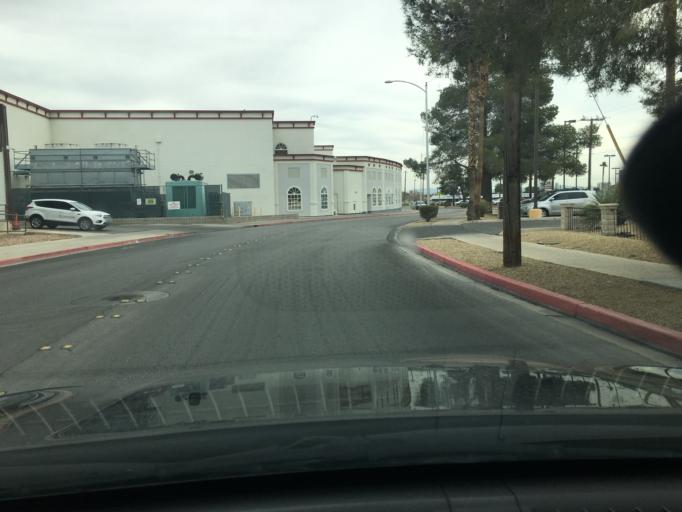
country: US
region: Nevada
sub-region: Clark County
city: Spring Valley
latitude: 36.1632
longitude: -115.2086
